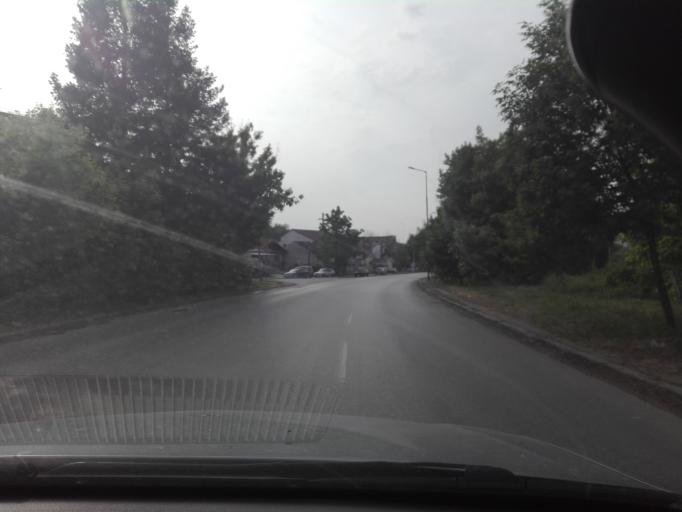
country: MK
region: Bitola
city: Bitola
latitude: 41.0148
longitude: 21.3455
